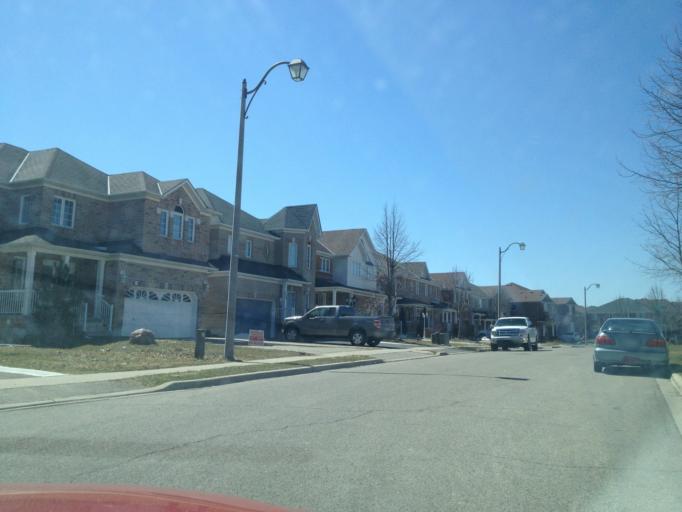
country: CA
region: Ontario
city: Brampton
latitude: 43.6849
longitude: -79.8131
